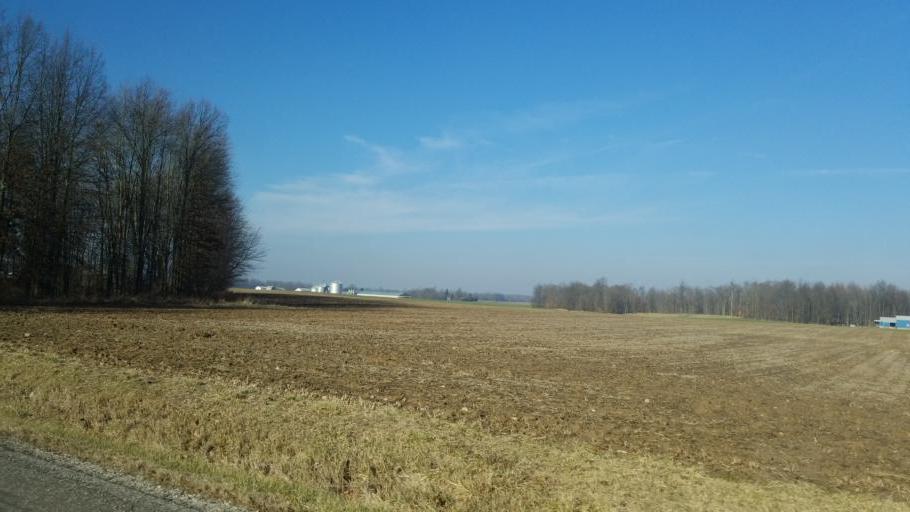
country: US
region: Ohio
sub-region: Crawford County
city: Bucyrus
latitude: 40.9066
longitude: -83.0665
